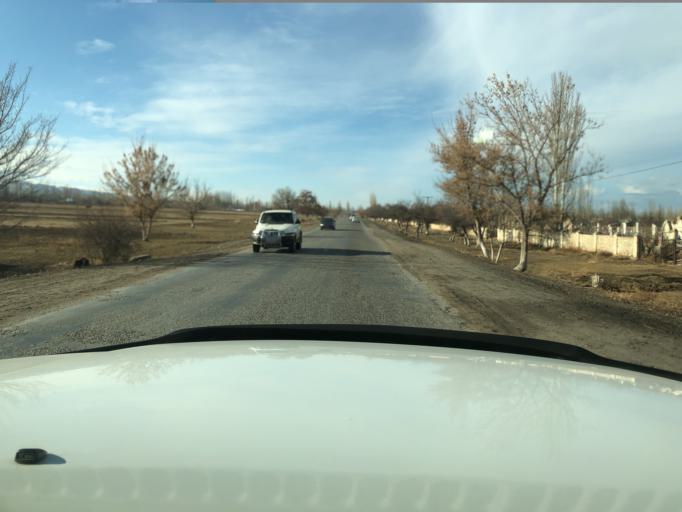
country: KG
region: Ysyk-Koel
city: Pokrovka
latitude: 42.3262
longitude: 77.9469
